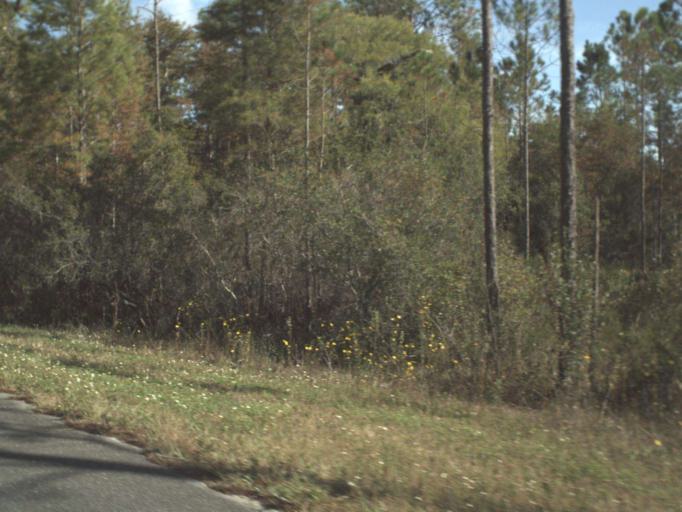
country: US
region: Florida
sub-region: Franklin County
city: Apalachicola
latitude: 29.9516
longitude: -84.9763
